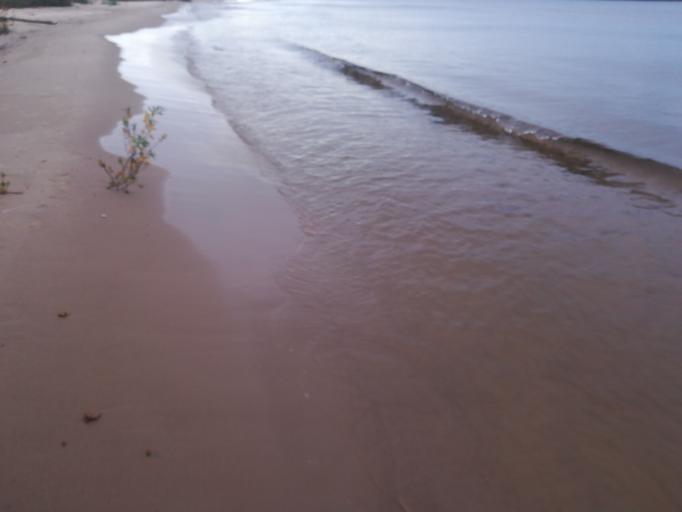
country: RU
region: Leningrad
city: Priozersk
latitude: 61.0398
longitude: 30.1941
